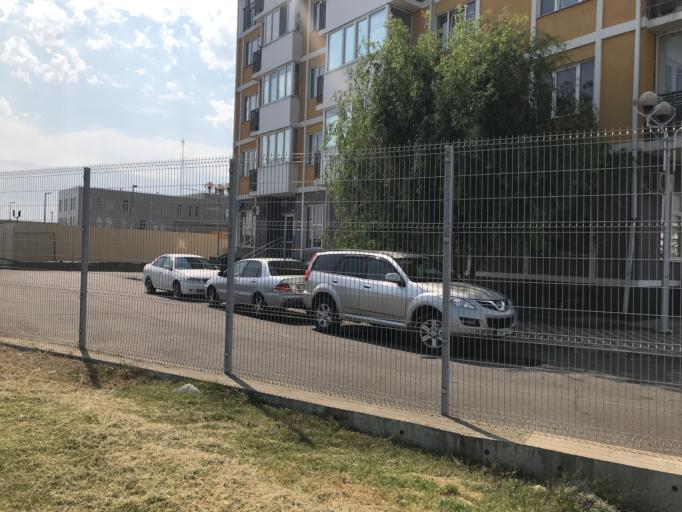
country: RU
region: Krasnodarskiy
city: Vysokoye
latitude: 43.4007
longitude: 39.9851
